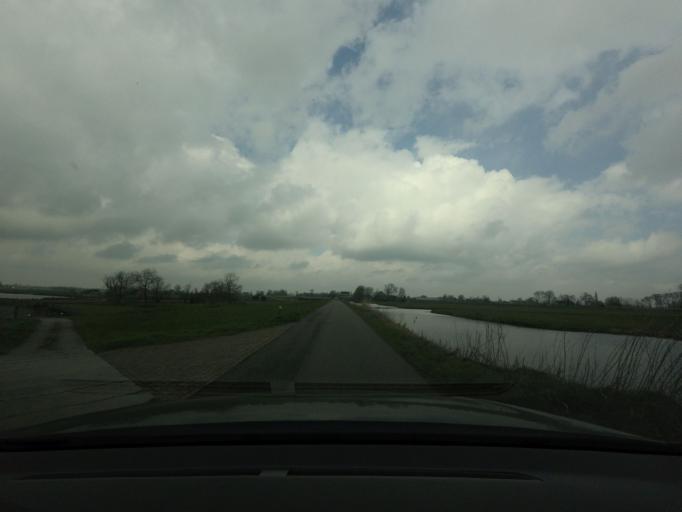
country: NL
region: Utrecht
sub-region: Gemeente De Ronde Venen
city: Mijdrecht
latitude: 52.1861
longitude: 4.8286
